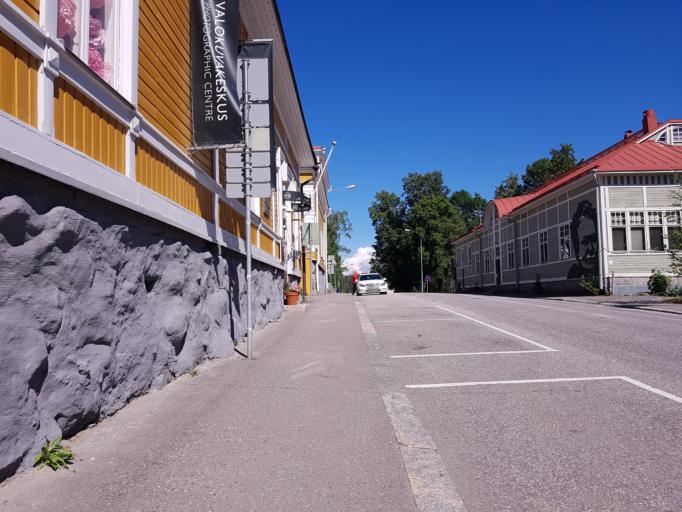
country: FI
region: Northern Savo
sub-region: Kuopio
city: Kuopio
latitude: 62.8903
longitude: 27.6856
